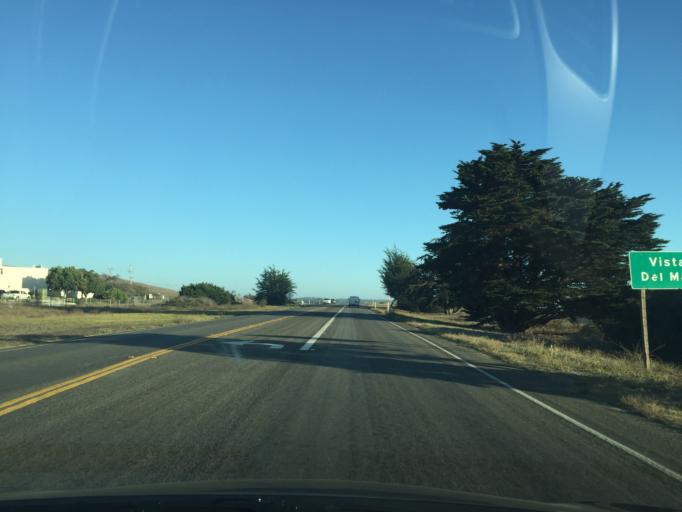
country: US
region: California
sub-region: San Luis Obispo County
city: Cambria
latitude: 35.6116
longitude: -121.1427
